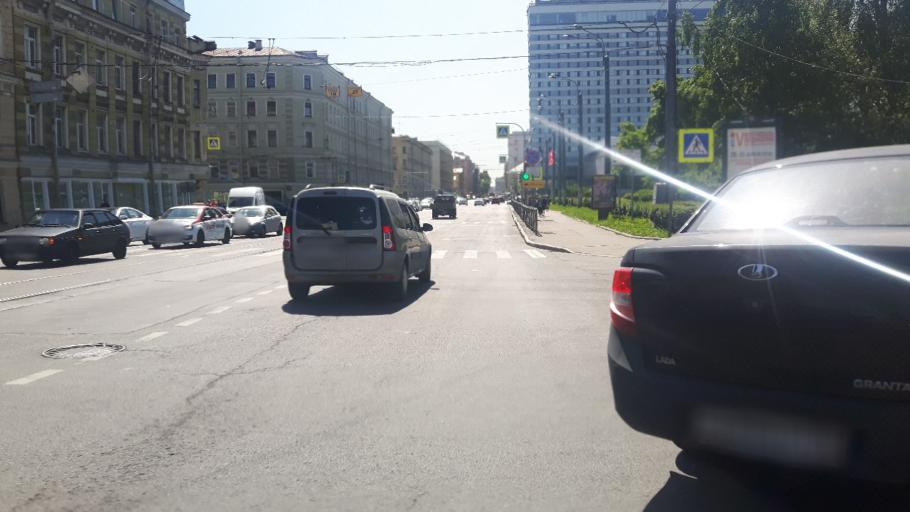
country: RU
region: St.-Petersburg
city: Admiralteisky
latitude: 59.9166
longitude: 30.2971
